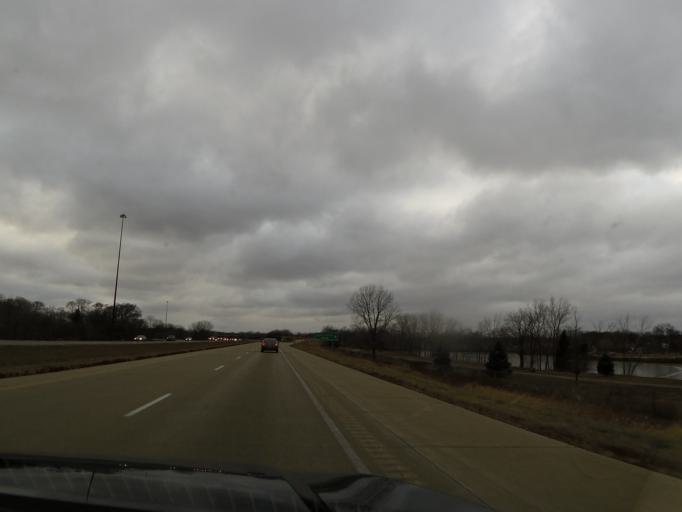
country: US
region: Iowa
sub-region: Black Hawk County
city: Evansdale
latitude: 42.4602
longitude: -92.2888
